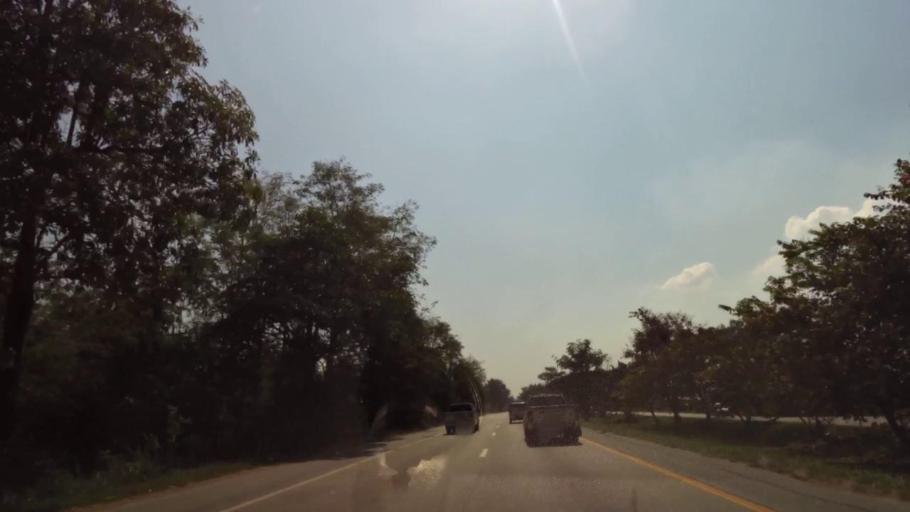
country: TH
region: Phichit
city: Wachira Barami
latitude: 16.5709
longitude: 100.1486
